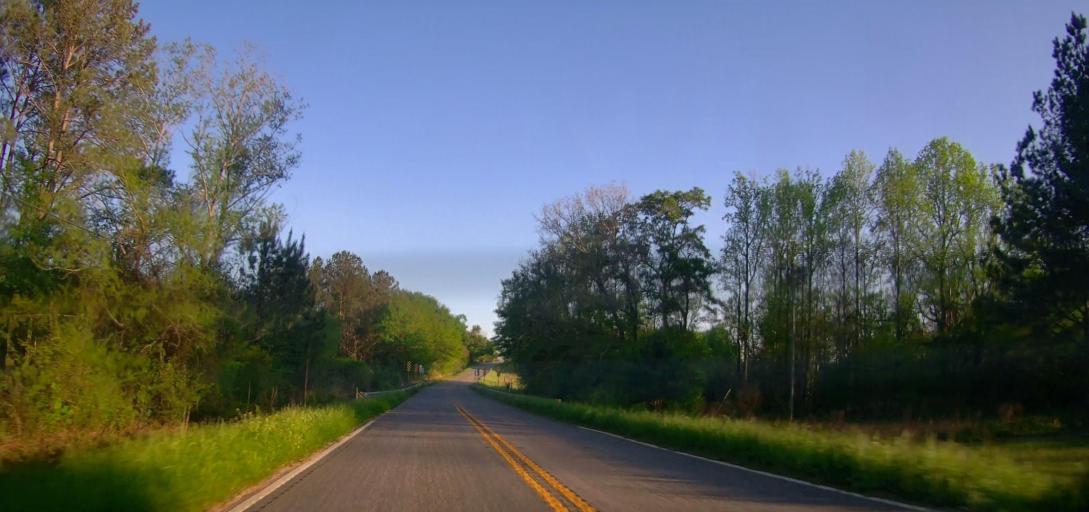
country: US
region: Georgia
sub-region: Marion County
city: Buena Vista
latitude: 32.3857
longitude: -84.4423
